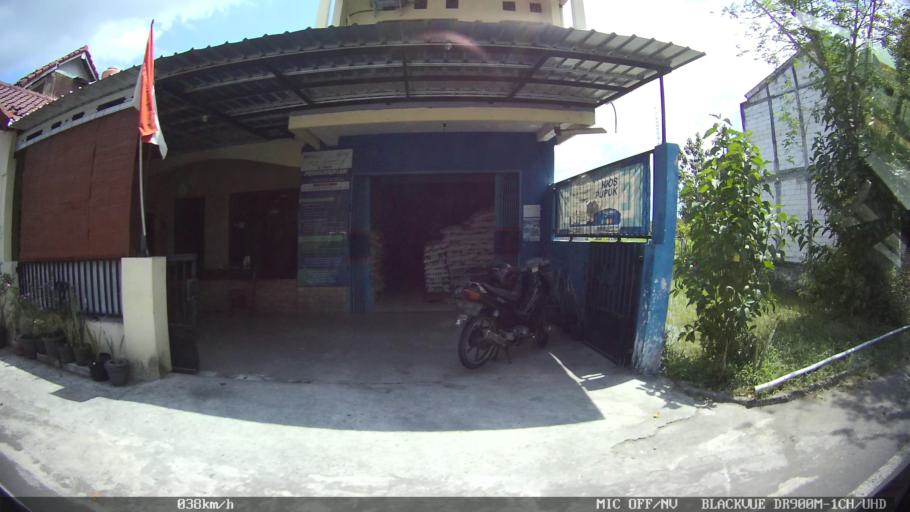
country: ID
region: Daerah Istimewa Yogyakarta
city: Bantul
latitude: -7.8851
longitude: 110.3354
